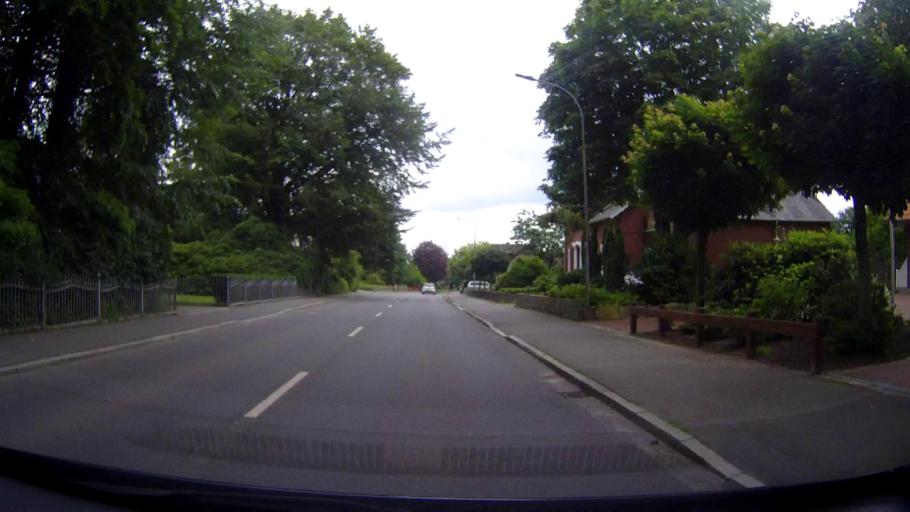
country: DE
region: Schleswig-Holstein
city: Hanerau-Hademarschen
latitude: 54.1211
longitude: 9.4316
